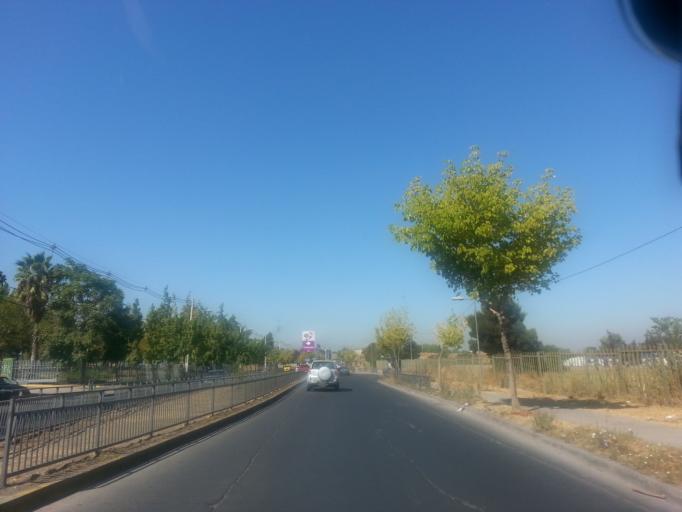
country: CL
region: Santiago Metropolitan
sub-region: Provincia de Santiago
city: Villa Presidente Frei, Nunoa, Santiago, Chile
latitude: -33.4595
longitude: -70.5465
